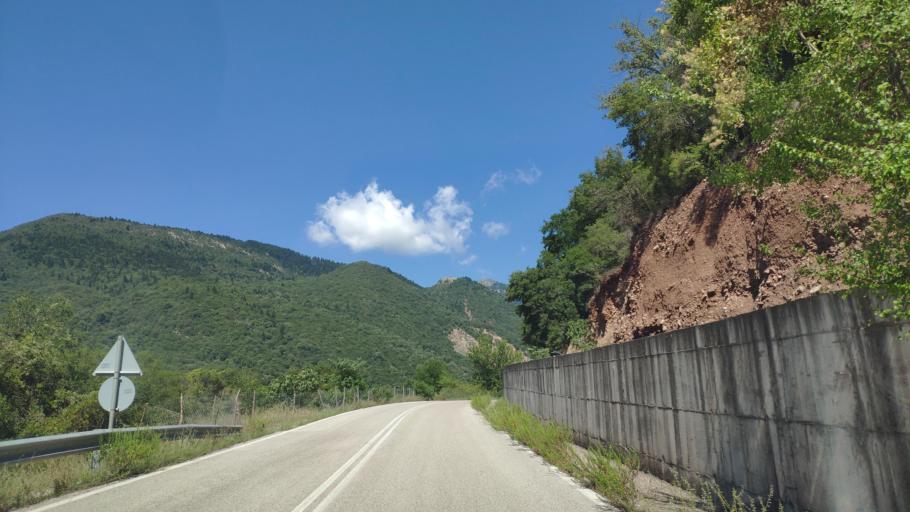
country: GR
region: Central Greece
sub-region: Nomos Evrytanias
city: Kerasochori
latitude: 39.0283
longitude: 21.6022
